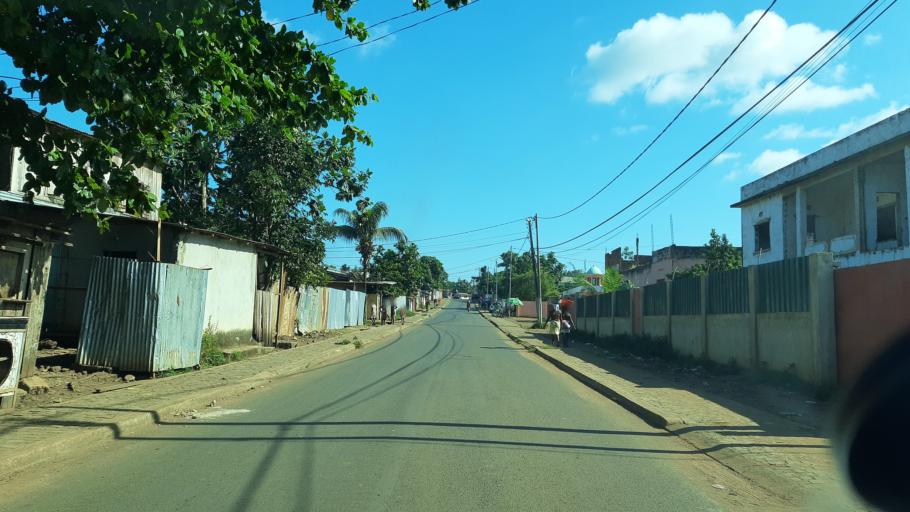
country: ST
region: Sao Tome Island
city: Sao Tome
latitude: 0.3227
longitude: 6.7286
